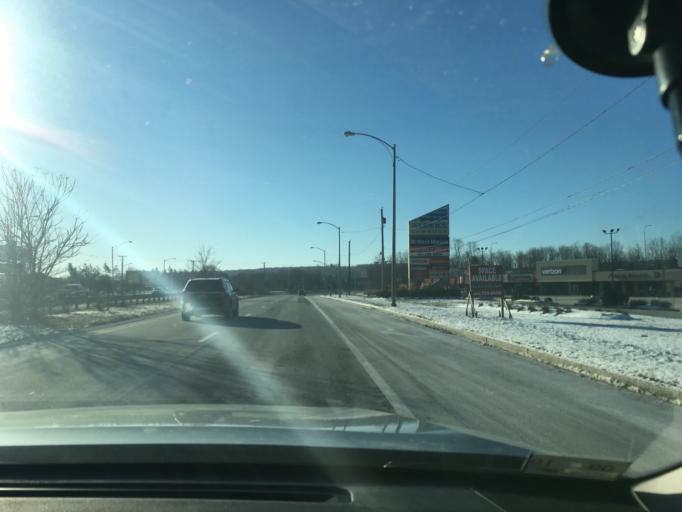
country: US
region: Rhode Island
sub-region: Kent County
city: West Warwick
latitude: 41.7274
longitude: -71.4804
